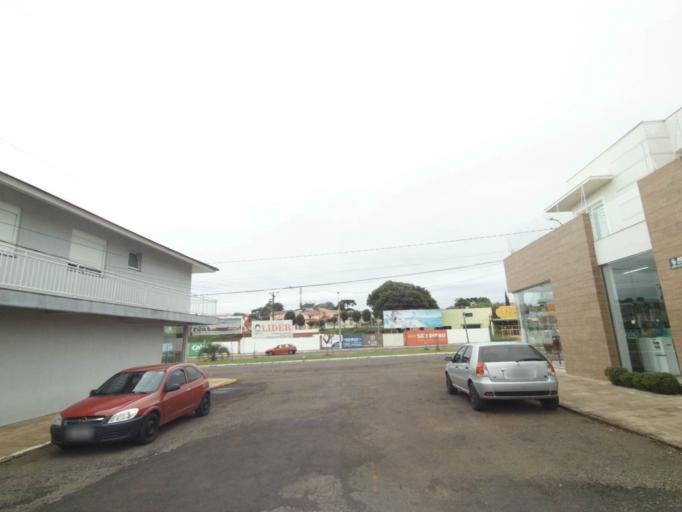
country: BR
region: Rio Grande do Sul
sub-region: Lagoa Vermelha
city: Lagoa Vermelha
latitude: -28.2131
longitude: -51.5143
